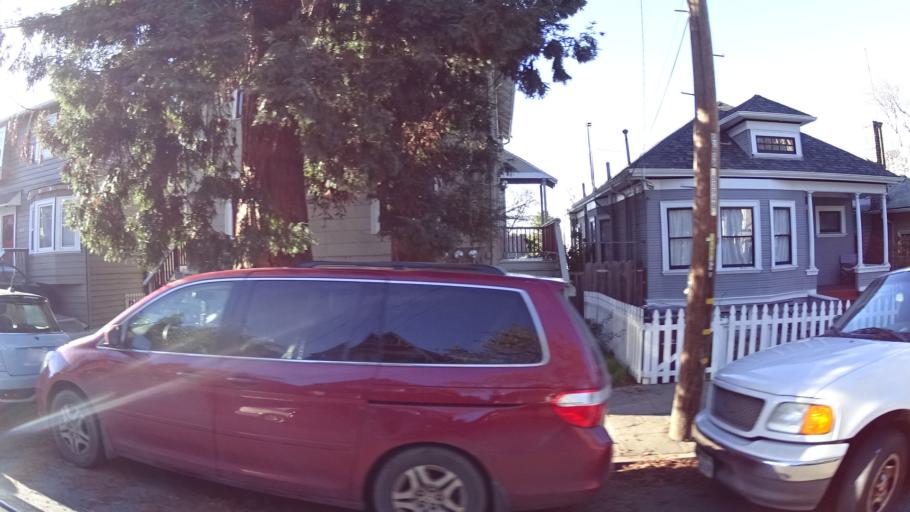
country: US
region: California
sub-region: Alameda County
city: Piedmont
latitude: 37.8292
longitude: -122.2546
